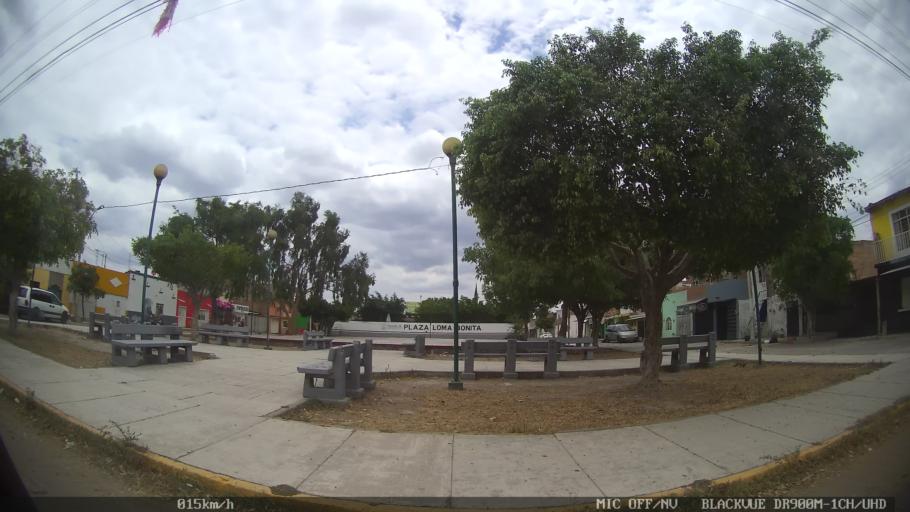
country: MX
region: Jalisco
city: Tonala
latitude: 20.6515
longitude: -103.2561
